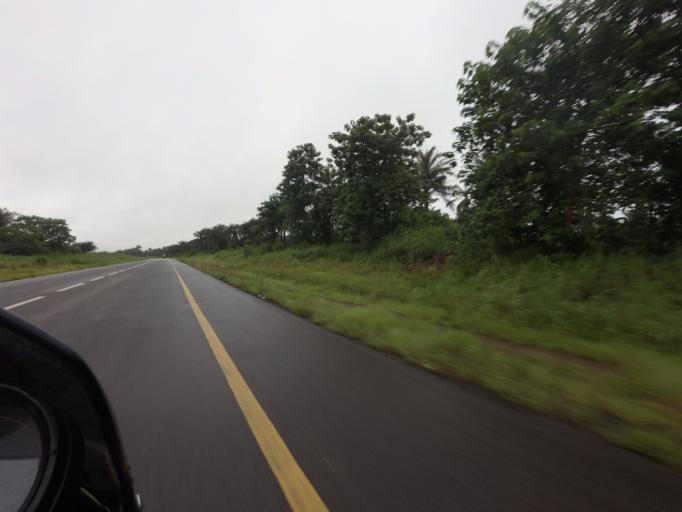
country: SL
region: Northern Province
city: Kambia
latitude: 9.0818
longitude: -12.9124
